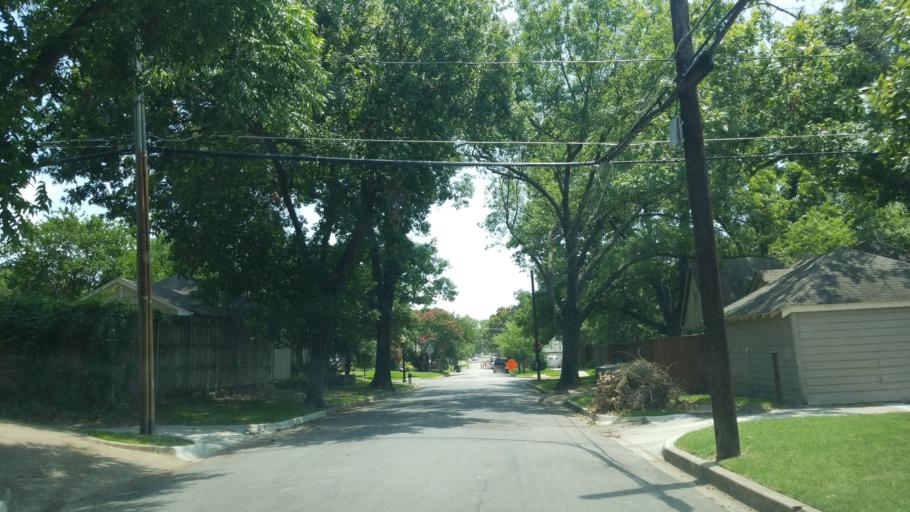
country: US
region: Texas
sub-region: Dallas County
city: Highland Park
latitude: 32.8288
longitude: -96.7774
